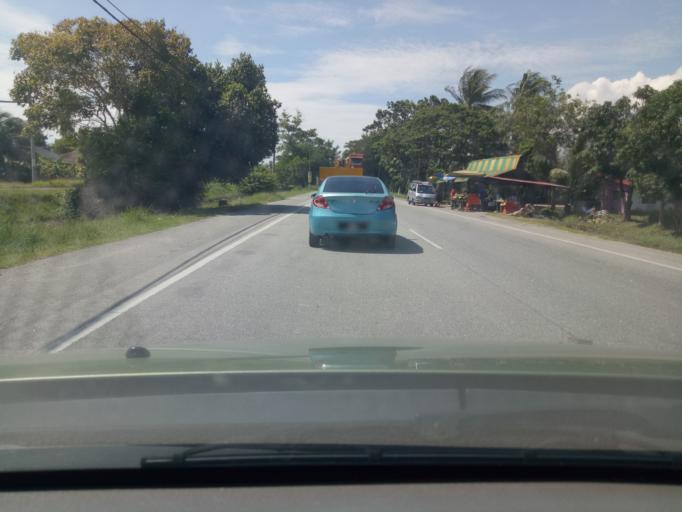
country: MY
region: Kedah
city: Gurun
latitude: 5.9639
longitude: 100.4038
